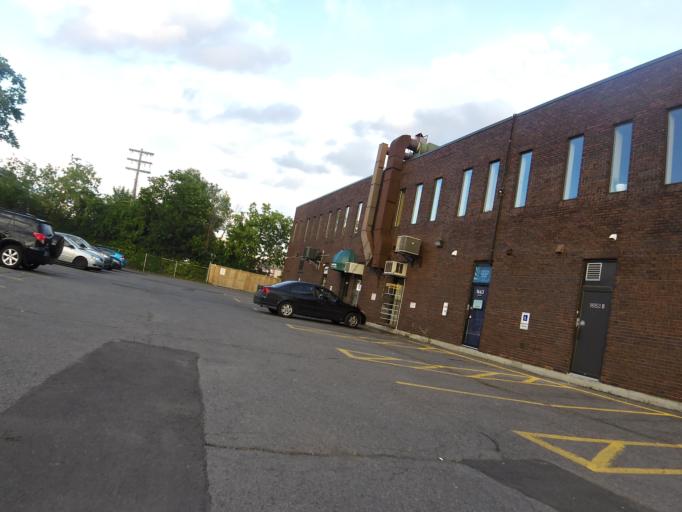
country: CA
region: Ontario
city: Ottawa
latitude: 45.3799
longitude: -75.7495
